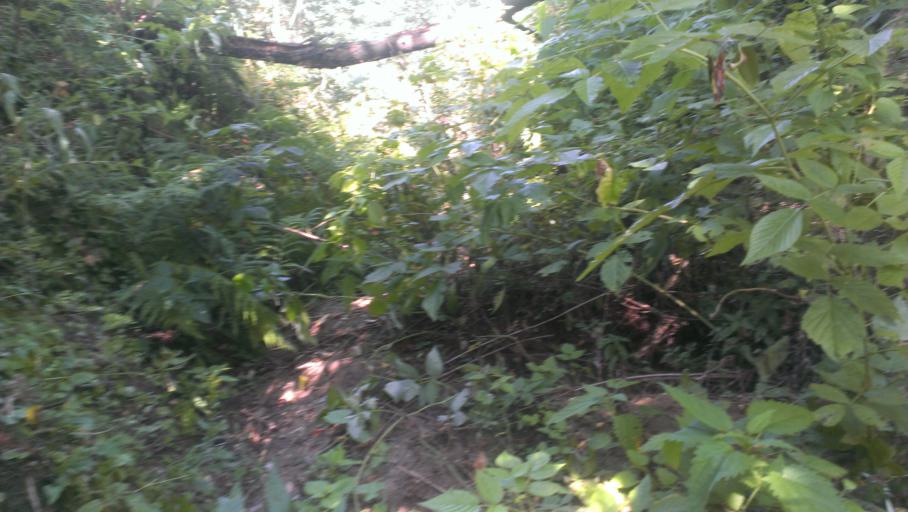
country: RU
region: Altai Krai
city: Nauchnyy Gorodok
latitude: 53.4245
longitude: 83.5048
